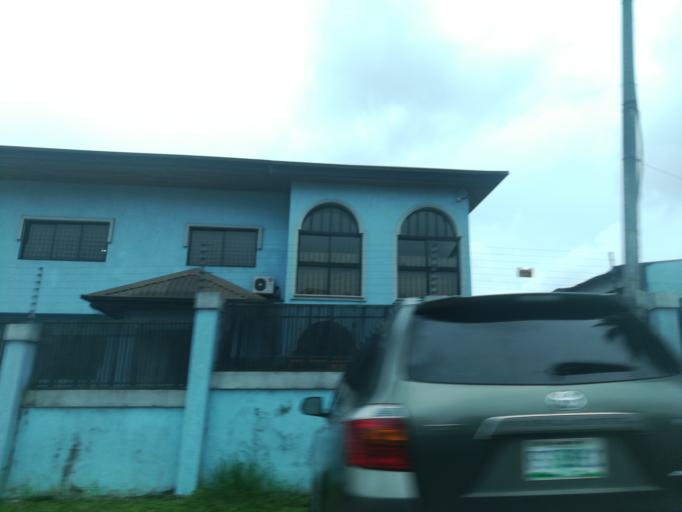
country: NG
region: Rivers
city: Port Harcourt
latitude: 4.8186
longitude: 6.9989
